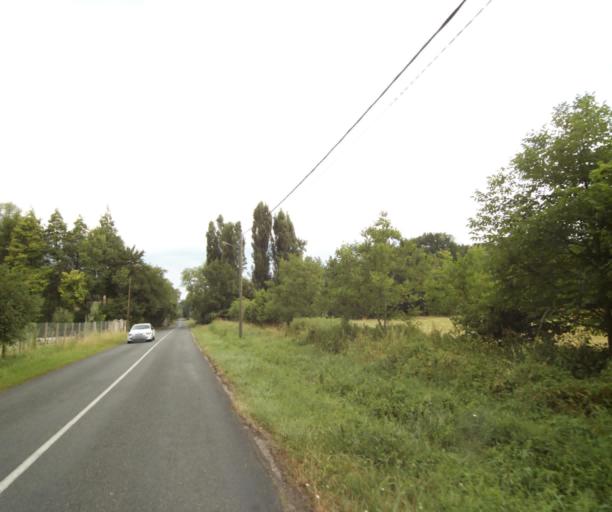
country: FR
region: Ile-de-France
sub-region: Departement de Seine-et-Marne
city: Cely
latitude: 48.4527
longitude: 2.5435
